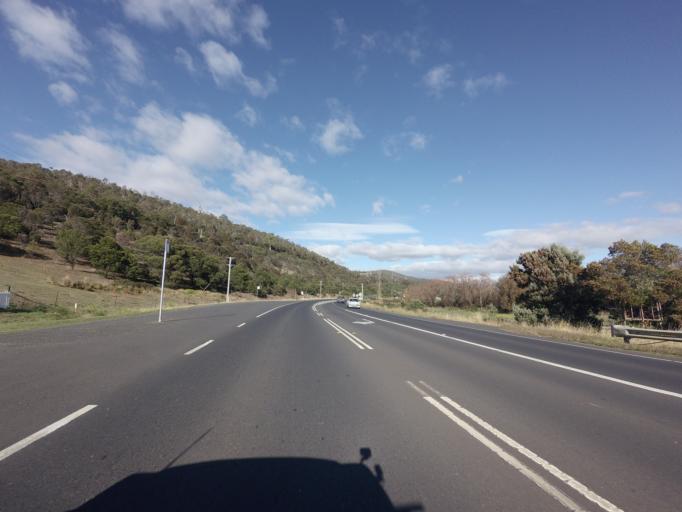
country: AU
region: Tasmania
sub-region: Derwent Valley
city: New Norfolk
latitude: -42.7826
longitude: 147.1076
